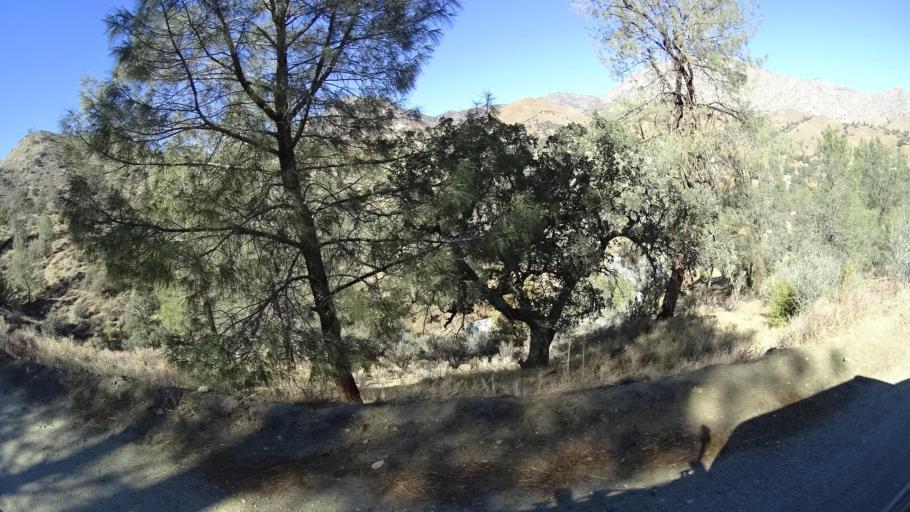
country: US
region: California
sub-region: Kern County
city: Wofford Heights
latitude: 35.7039
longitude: -118.4766
